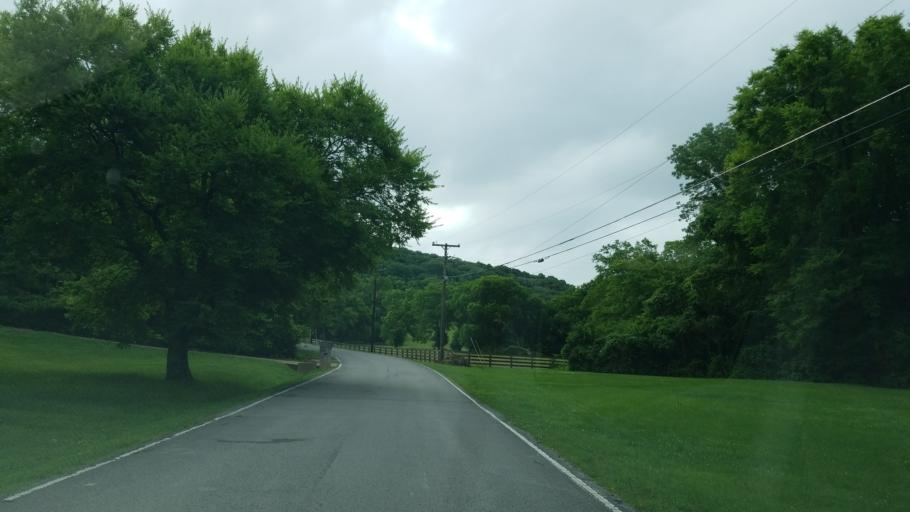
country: US
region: Tennessee
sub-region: Williamson County
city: Brentwood
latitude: 36.0480
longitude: -86.8111
